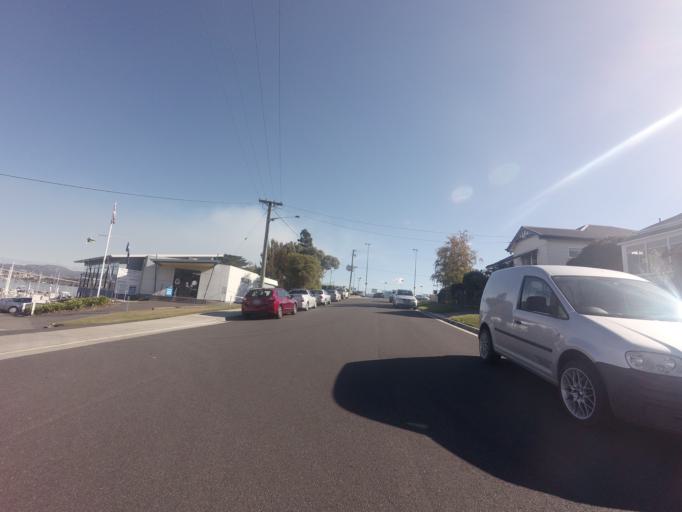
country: AU
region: Tasmania
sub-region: Clarence
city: Lindisfarne
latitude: -42.8509
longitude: 147.3528
